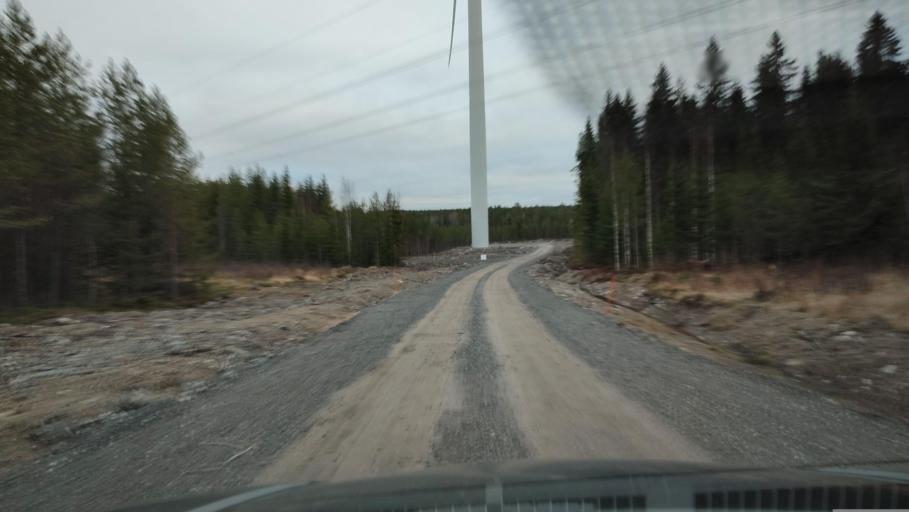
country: FI
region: Southern Ostrobothnia
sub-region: Suupohja
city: Karijoki
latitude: 62.2000
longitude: 21.5917
